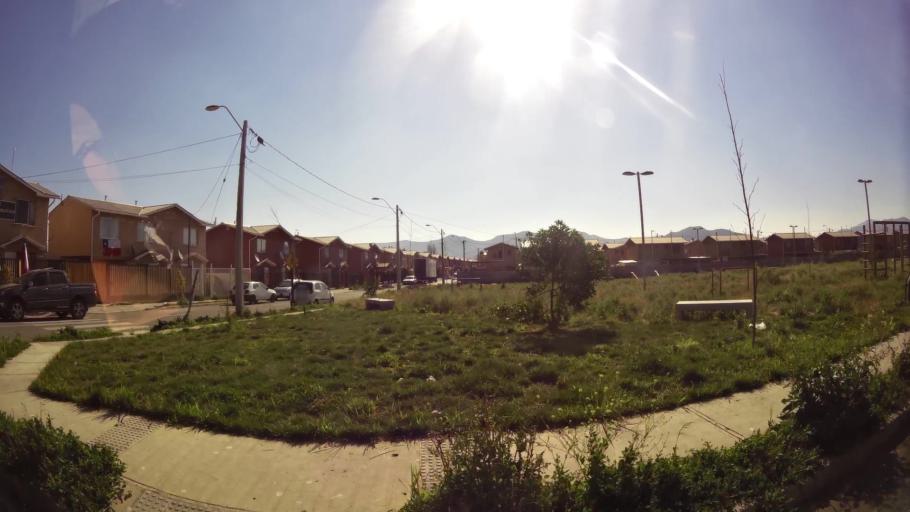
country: CL
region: Santiago Metropolitan
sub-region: Provincia de Talagante
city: Penaflor
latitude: -33.6180
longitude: -70.8776
